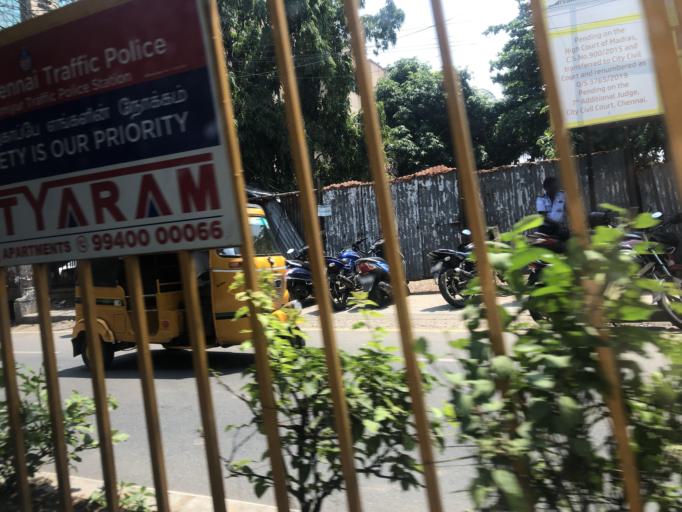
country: IN
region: Tamil Nadu
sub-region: Chennai
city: Gandhi Nagar
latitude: 12.9958
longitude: 80.2558
